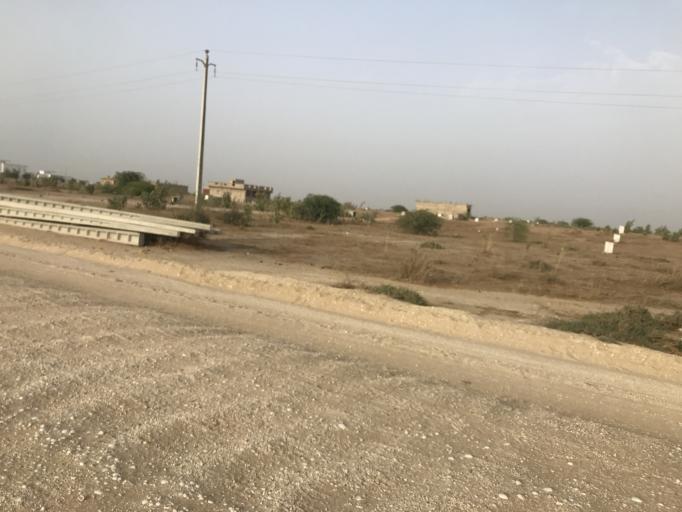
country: SN
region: Saint-Louis
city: Saint-Louis
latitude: 16.0259
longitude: -16.4457
